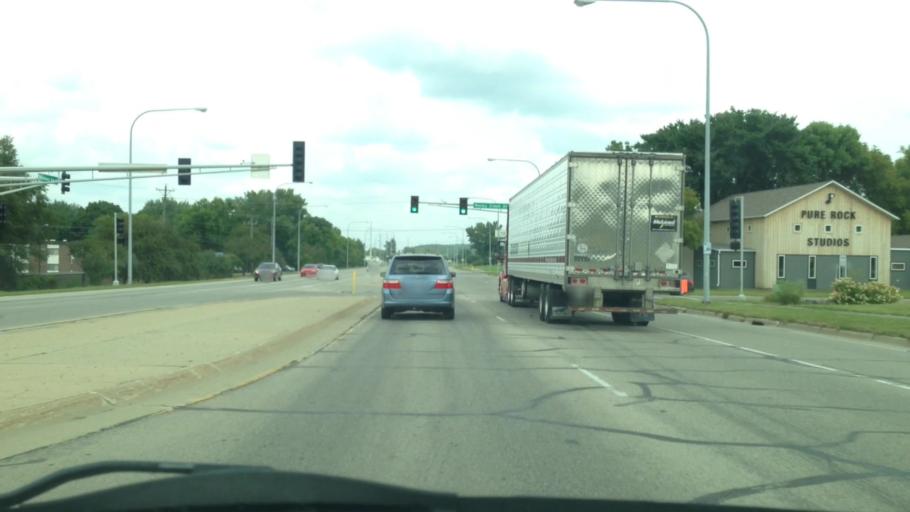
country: US
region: Minnesota
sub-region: Olmsted County
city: Rochester
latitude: 44.0540
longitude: -92.4548
